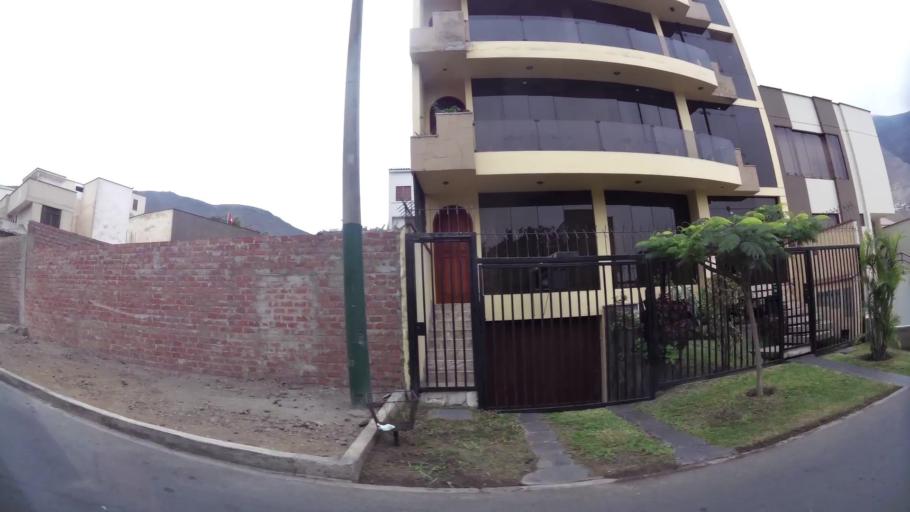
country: PE
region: Lima
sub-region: Lima
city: La Molina
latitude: -12.1045
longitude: -76.9568
